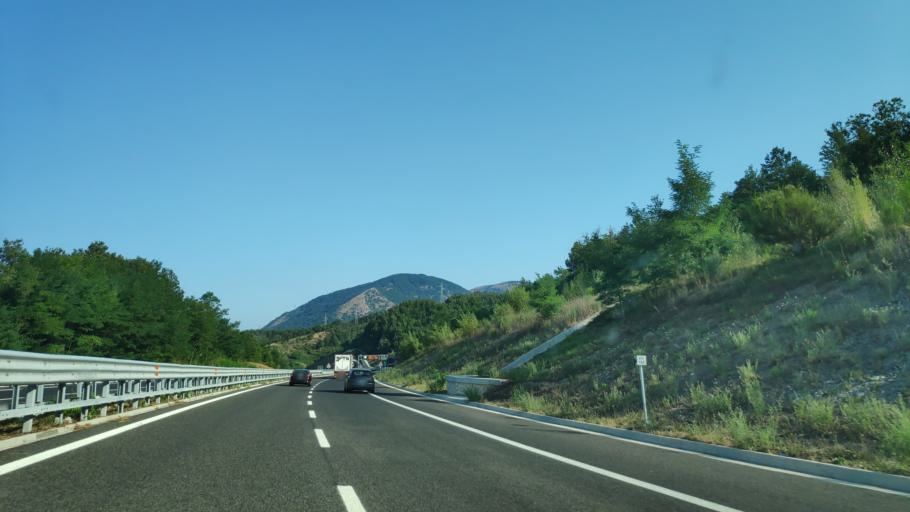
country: IT
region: Basilicate
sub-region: Provincia di Potenza
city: Nemoli
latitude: 40.1047
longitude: 15.7960
